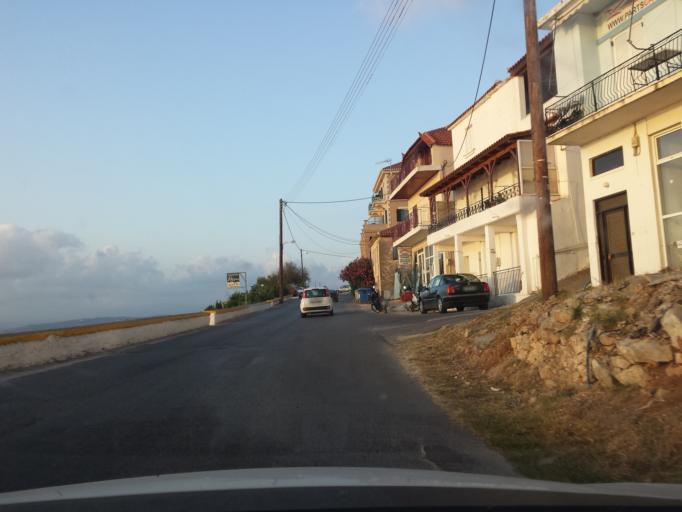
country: GR
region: Peloponnese
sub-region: Nomos Messinias
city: Pylos
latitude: 36.9185
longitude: 21.7019
